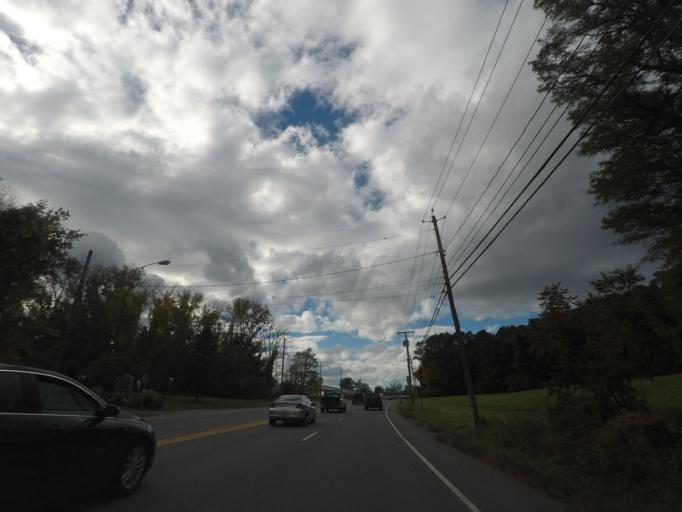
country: US
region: New York
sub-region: Albany County
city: Westmere
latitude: 42.7068
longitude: -73.9198
